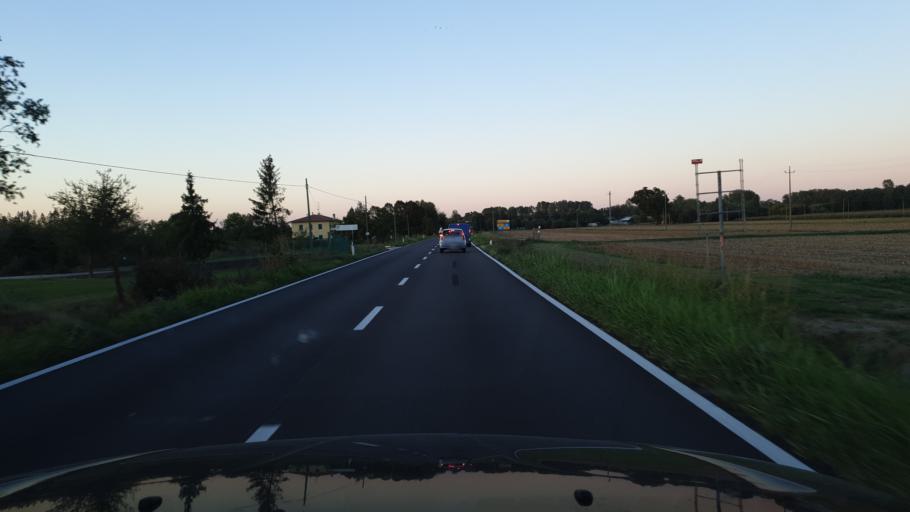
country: IT
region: Emilia-Romagna
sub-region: Provincia di Bologna
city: Ca De Fabbri
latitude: 44.5920
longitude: 11.4332
